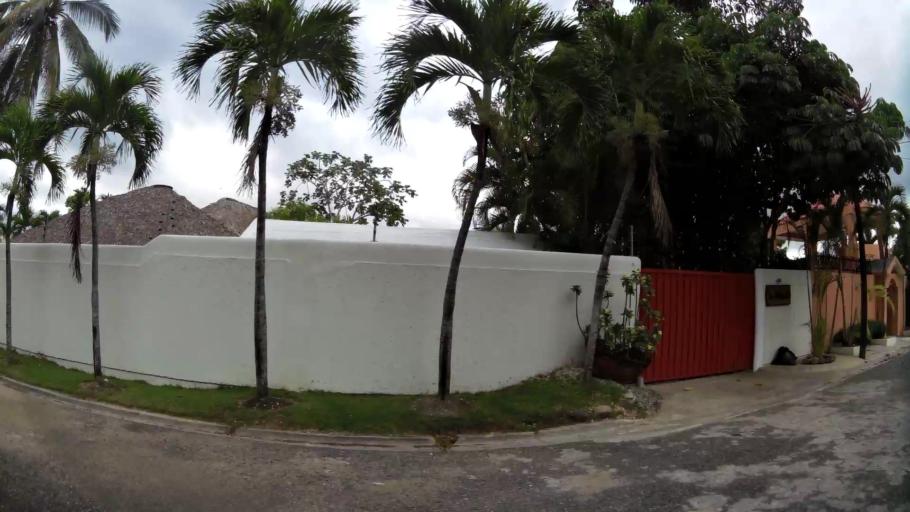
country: DO
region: Nacional
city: La Agustina
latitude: 18.5039
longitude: -69.9347
